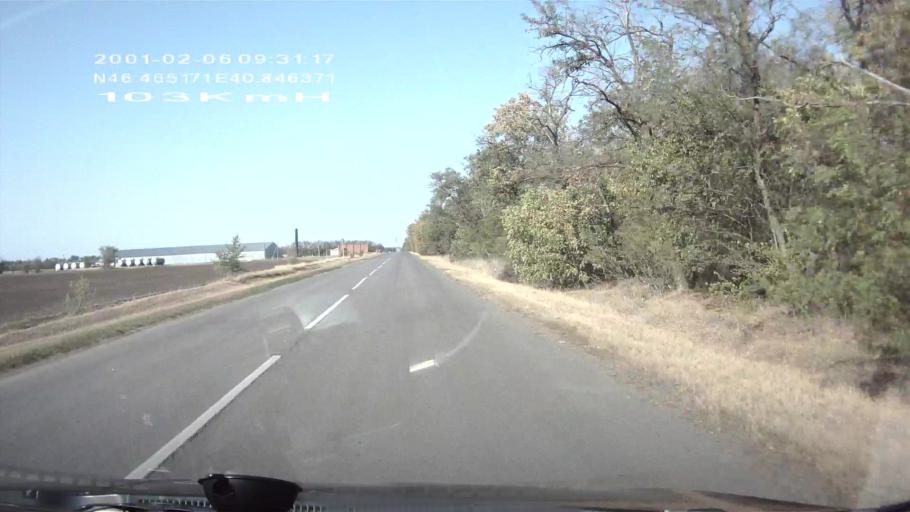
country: RU
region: Rostov
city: Tselina
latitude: 46.4652
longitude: 40.8451
